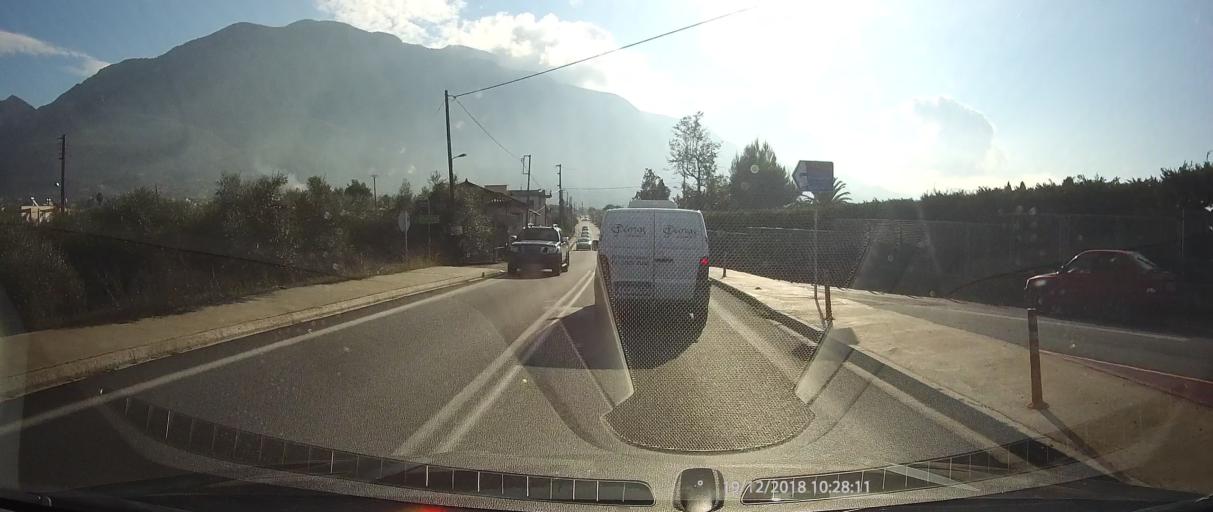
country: GR
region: Peloponnese
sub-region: Nomos Messinias
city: Paralia Vergas
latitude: 37.0293
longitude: 22.1394
